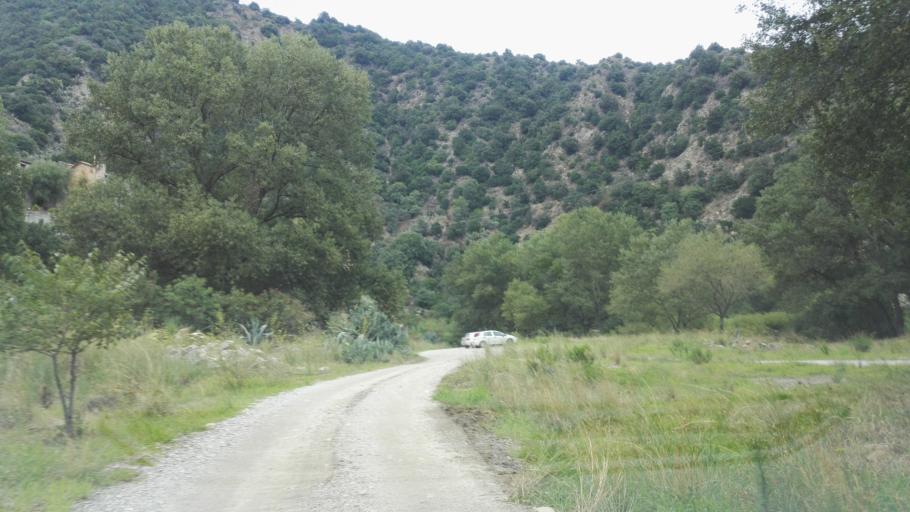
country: IT
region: Calabria
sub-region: Provincia di Reggio Calabria
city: Caulonia
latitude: 38.4236
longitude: 16.3770
